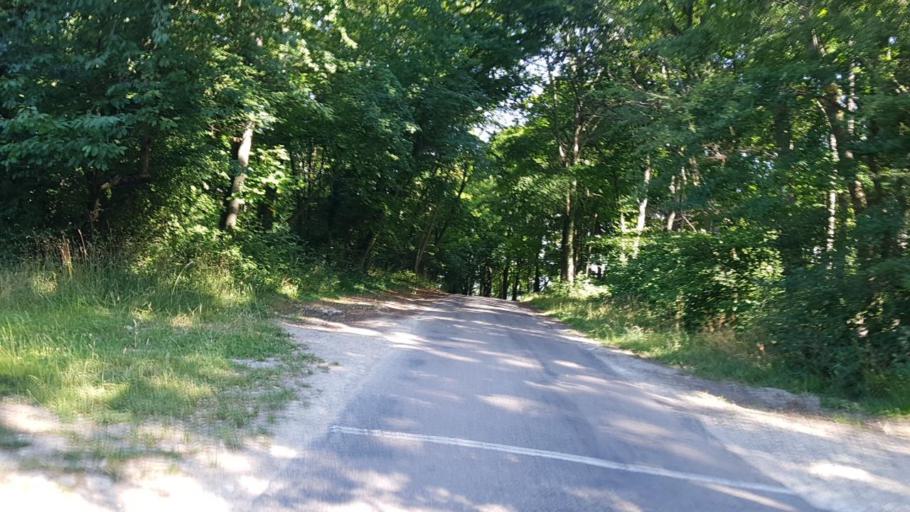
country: FR
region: Picardie
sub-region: Departement de l'Oise
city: Pontpoint
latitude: 49.2949
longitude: 2.6459
